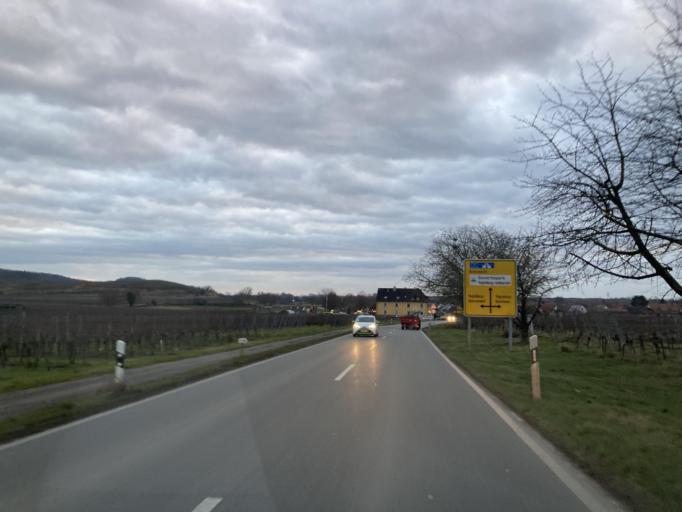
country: DE
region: Baden-Wuerttemberg
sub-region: Freiburg Region
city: Vogtsburg
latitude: 48.1020
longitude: 7.6073
